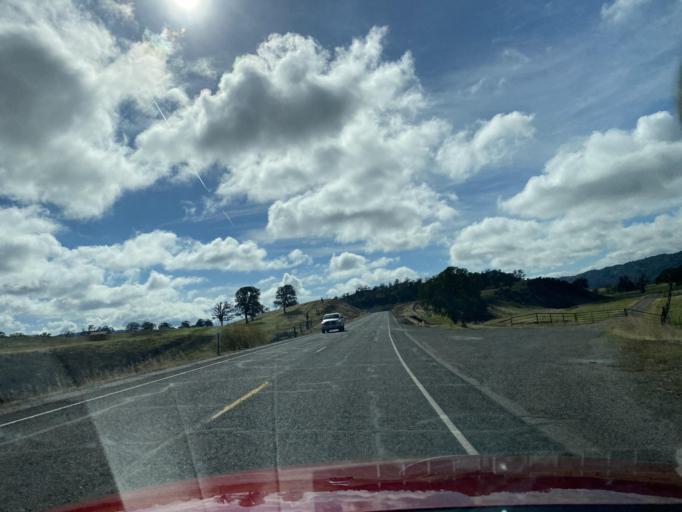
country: US
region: California
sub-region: Glenn County
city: Willows
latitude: 39.5421
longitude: -122.5354
